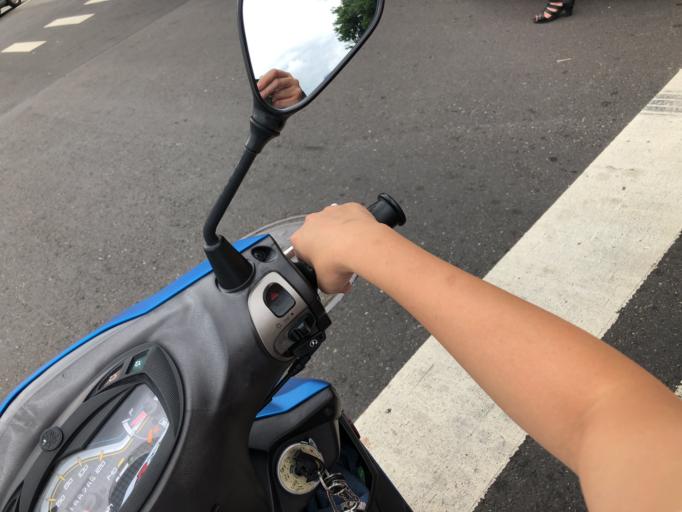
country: TW
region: Taiwan
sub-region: Changhua
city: Chang-hua
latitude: 24.1027
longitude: 120.6188
